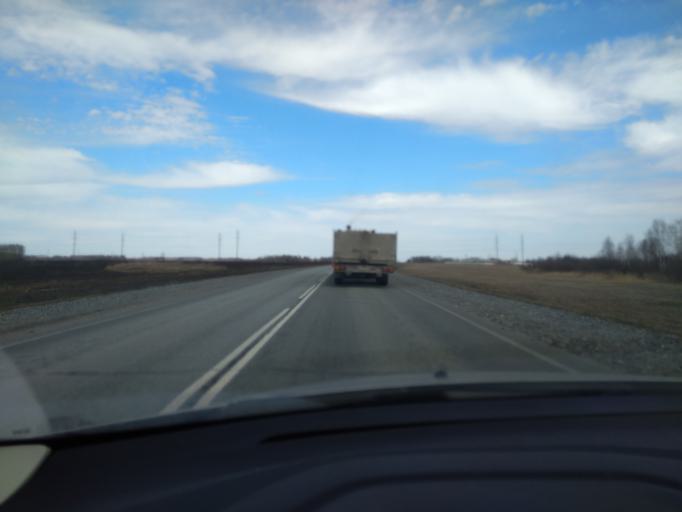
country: RU
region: Sverdlovsk
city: Pyshma
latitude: 56.9789
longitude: 63.2400
